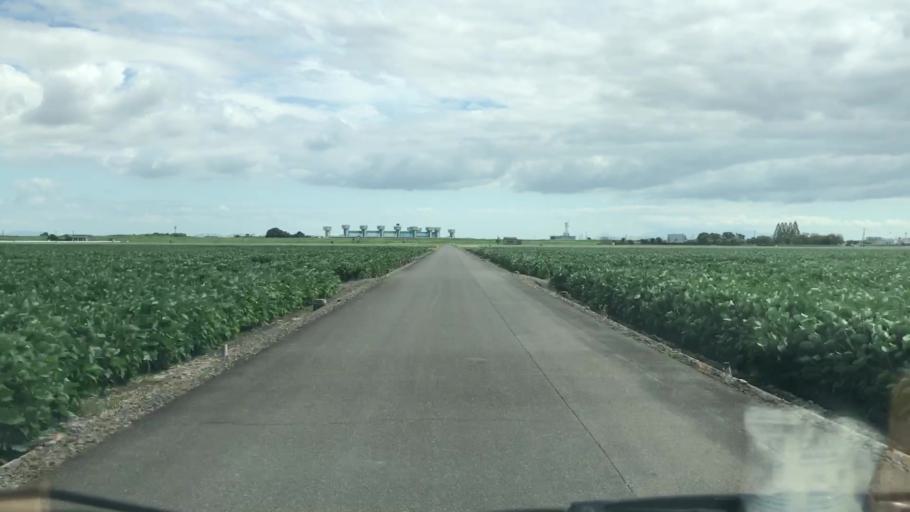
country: JP
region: Saga Prefecture
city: Saga-shi
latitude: 33.2132
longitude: 130.1834
